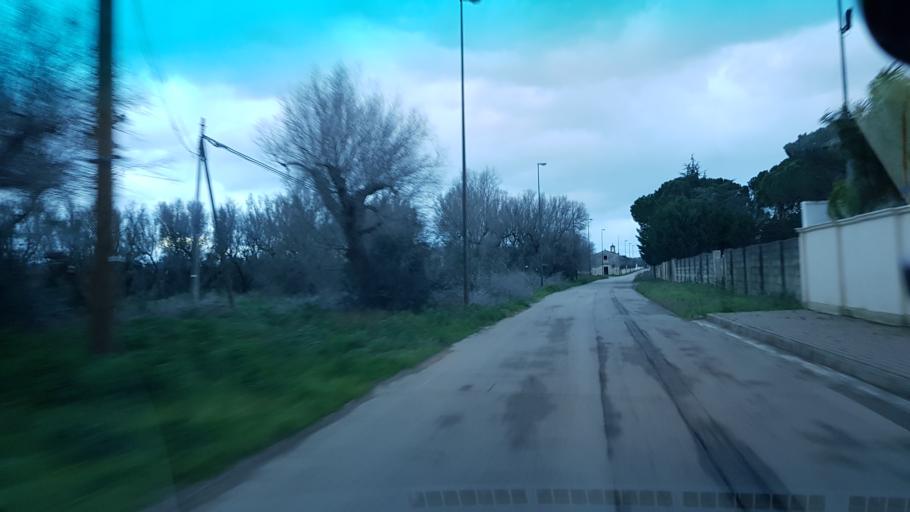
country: IT
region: Apulia
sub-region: Provincia di Brindisi
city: Torchiarolo
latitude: 40.4933
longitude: 18.0543
